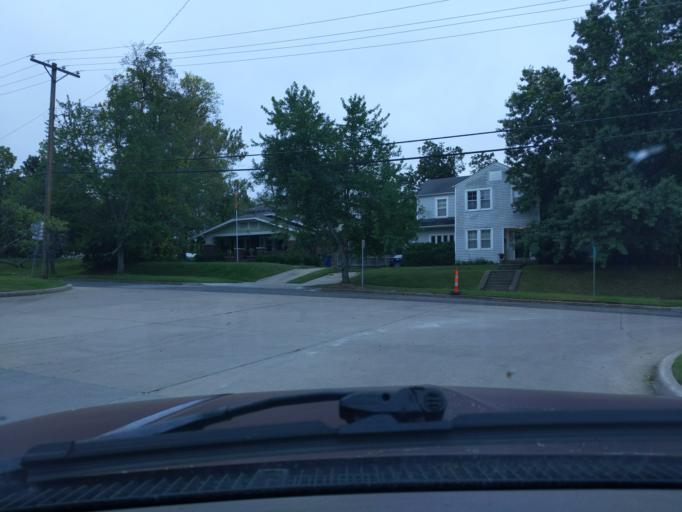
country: US
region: Oklahoma
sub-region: Tulsa County
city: Tulsa
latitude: 36.1353
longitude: -95.9702
